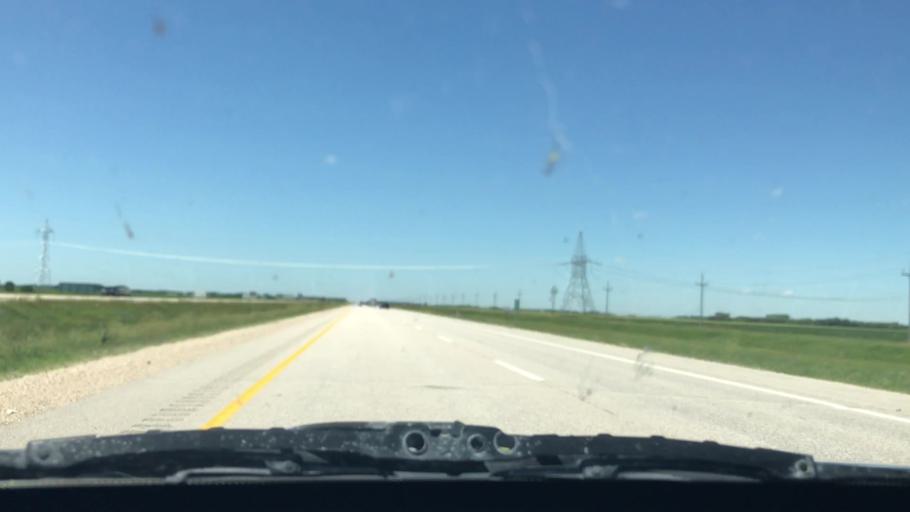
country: CA
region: Manitoba
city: Steinbach
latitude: 49.7102
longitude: -96.6691
